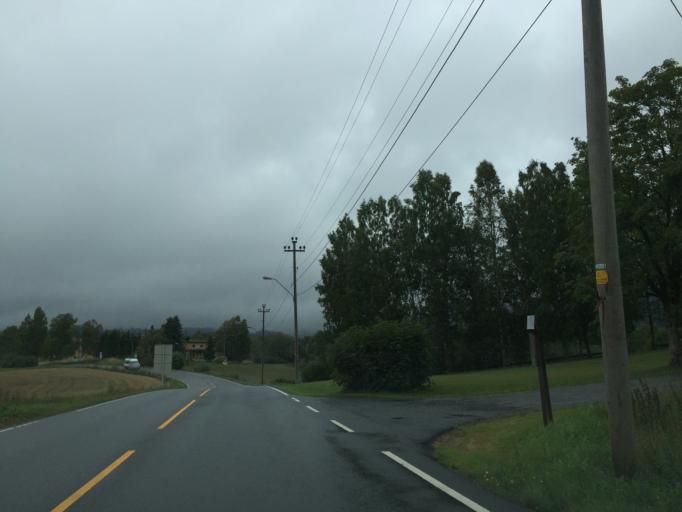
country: NO
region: Akershus
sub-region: Baerum
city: Lysaker
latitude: 60.0151
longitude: 10.6151
